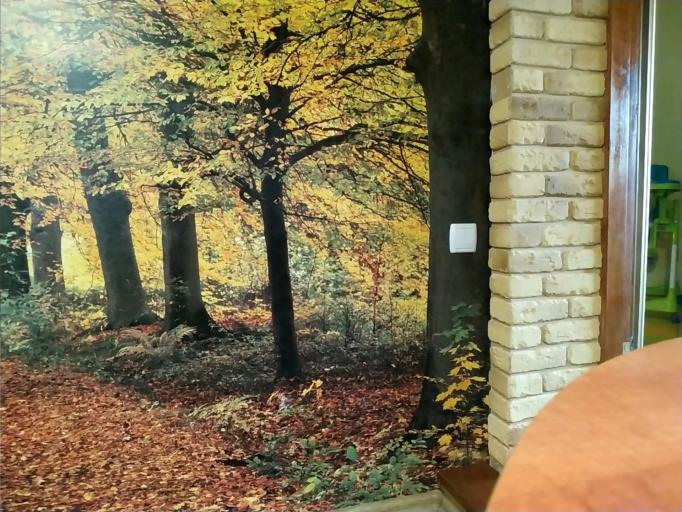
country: RU
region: Leningrad
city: Tolmachevo
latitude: 58.9289
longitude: 29.7248
